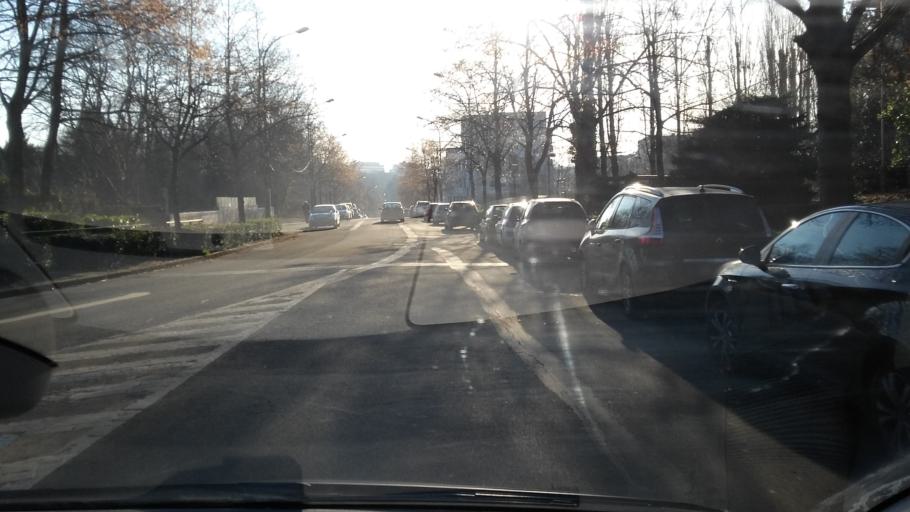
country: BE
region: Brussels Capital
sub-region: Bruxelles-Capitale
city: Brussels
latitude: 50.8046
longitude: 4.3944
